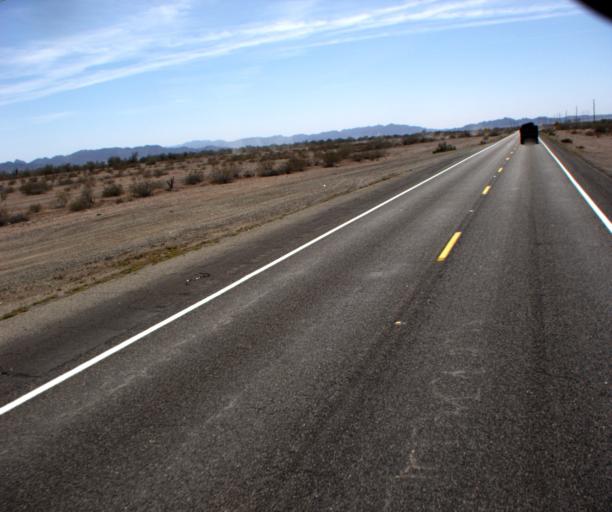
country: US
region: Arizona
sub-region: Yuma County
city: Fortuna Foothills
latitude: 32.9214
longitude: -114.3194
